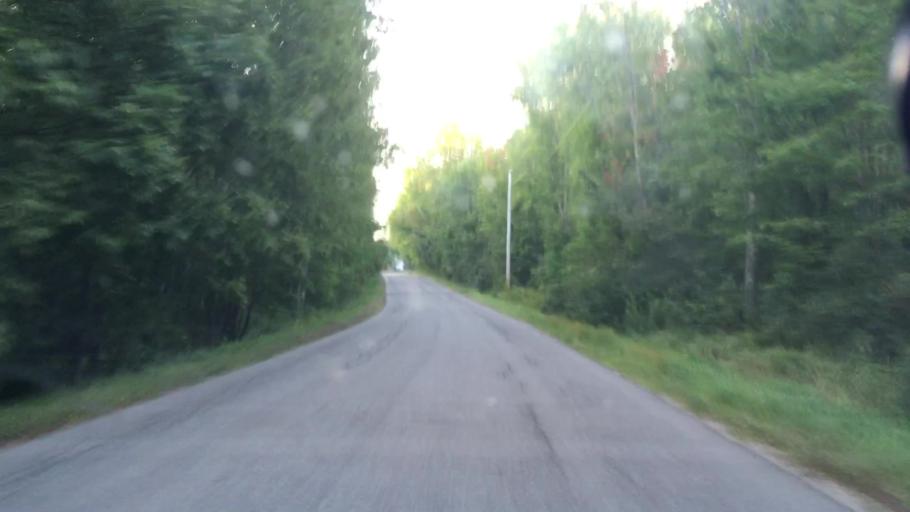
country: US
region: Maine
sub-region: Waldo County
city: Frankfort
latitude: 44.6696
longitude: -68.9259
